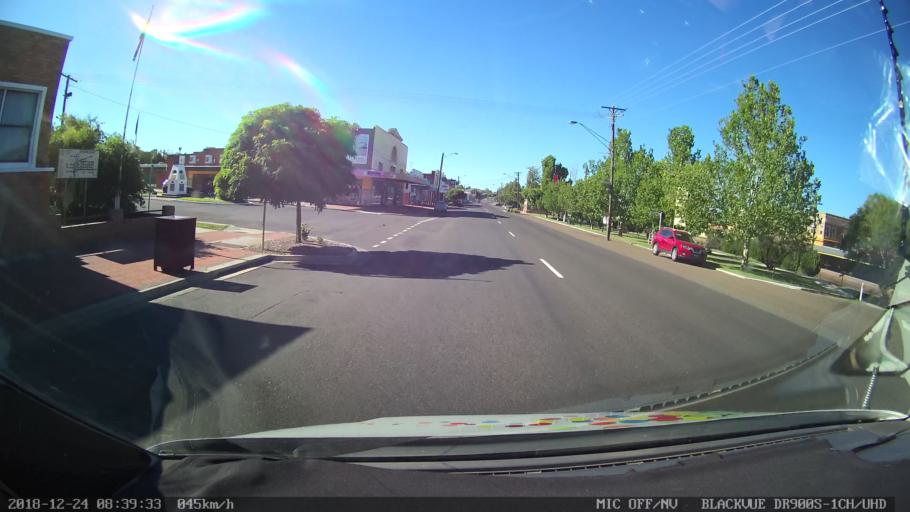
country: AU
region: New South Wales
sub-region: Liverpool Plains
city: Quirindi
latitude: -31.3488
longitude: 150.6472
